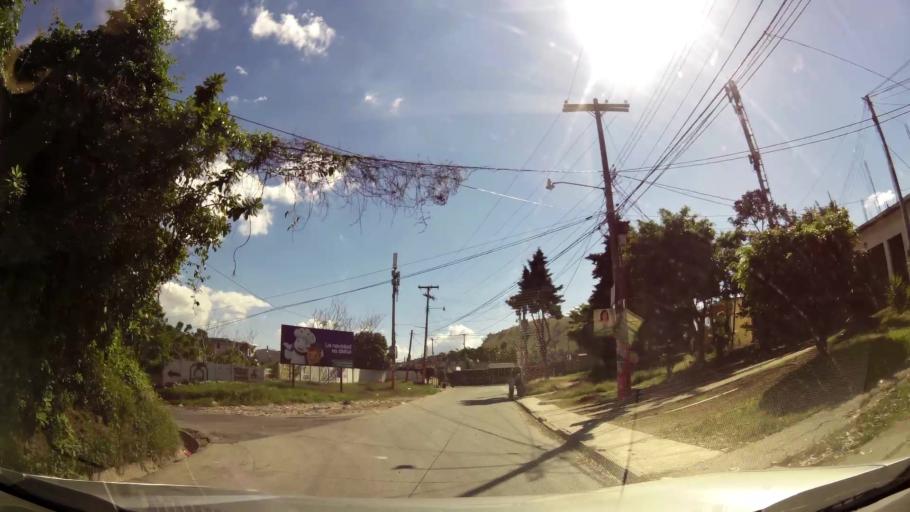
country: GT
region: Guatemala
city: Petapa
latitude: 14.4977
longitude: -90.5630
